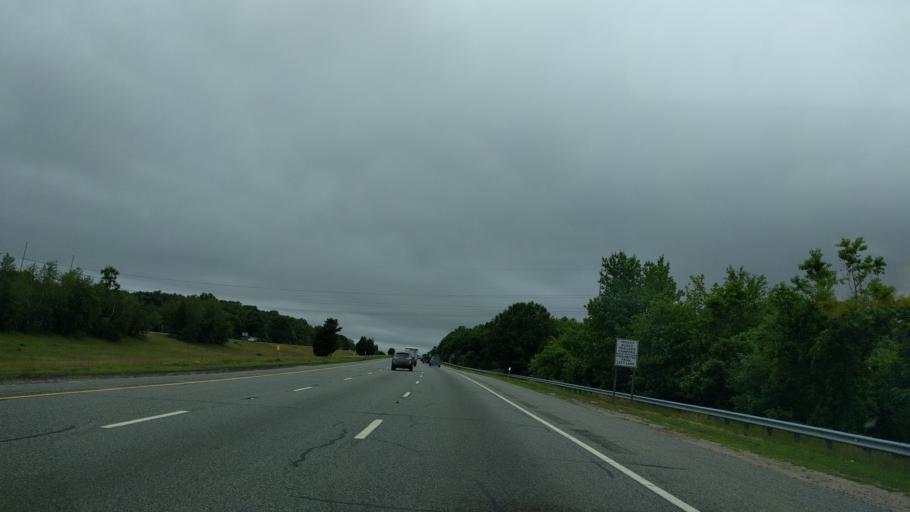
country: US
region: Rhode Island
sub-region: Providence County
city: Cumberland Hill
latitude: 41.9417
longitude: -71.4847
